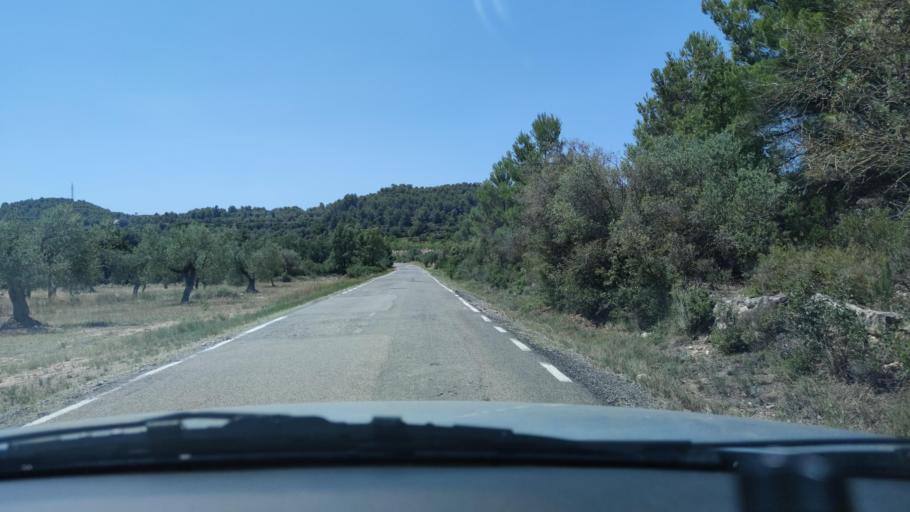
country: ES
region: Catalonia
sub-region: Provincia de Lleida
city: Fulleda
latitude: 41.4737
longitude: 1.0214
